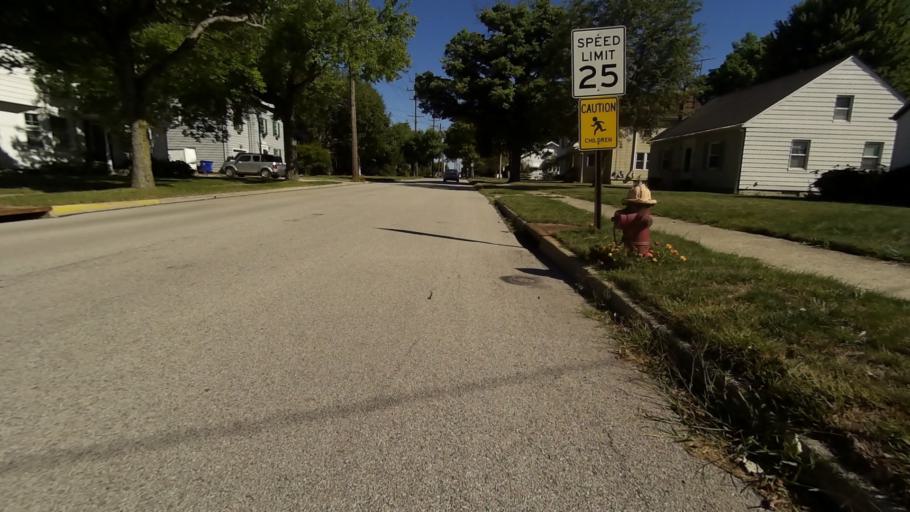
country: US
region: Ohio
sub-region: Portage County
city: Kent
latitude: 41.1485
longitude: -81.3775
